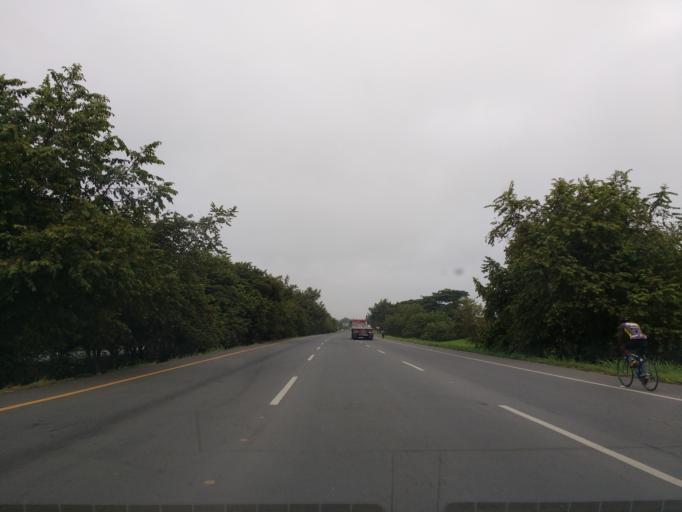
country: CO
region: Valle del Cauca
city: Palmira
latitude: 3.5215
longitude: -76.3519
